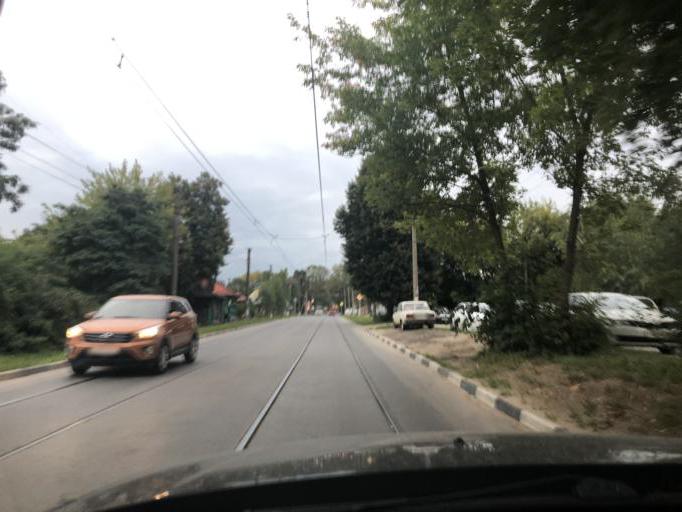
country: RU
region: Tula
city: Tula
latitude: 54.2048
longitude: 37.6496
